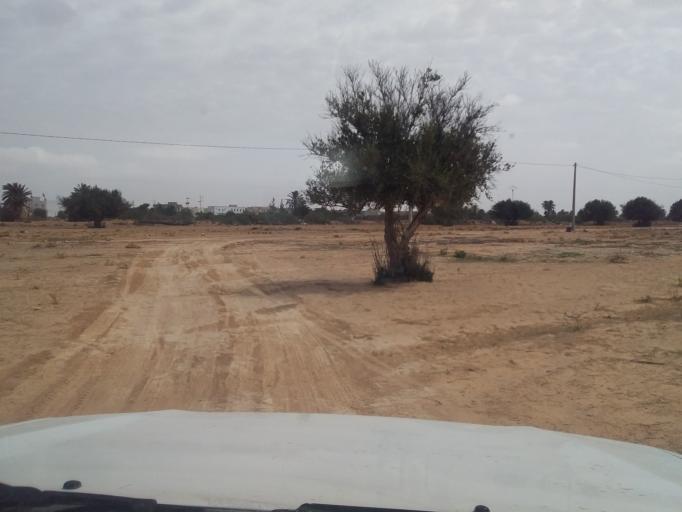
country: TN
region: Qabis
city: Matmata
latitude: 33.6197
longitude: 10.2665
